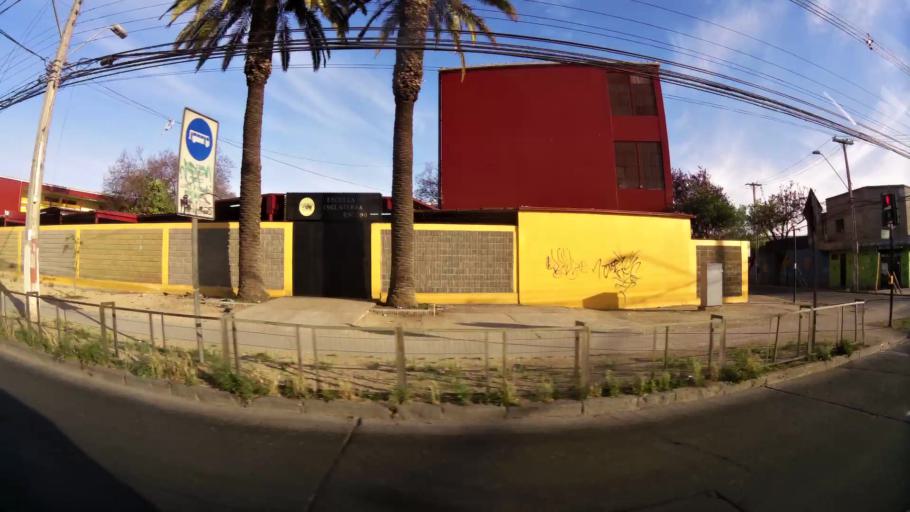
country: CL
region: Santiago Metropolitan
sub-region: Provincia de Santiago
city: Lo Prado
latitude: -33.4408
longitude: -70.7041
